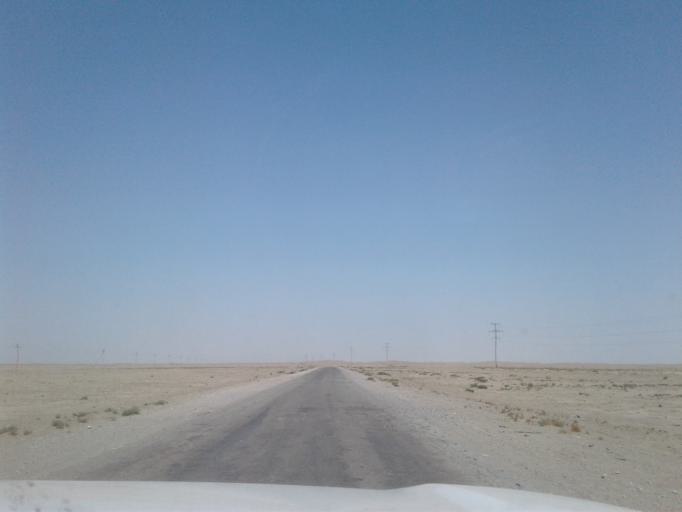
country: TM
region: Balkan
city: Gumdag
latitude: 38.3584
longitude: 54.3778
